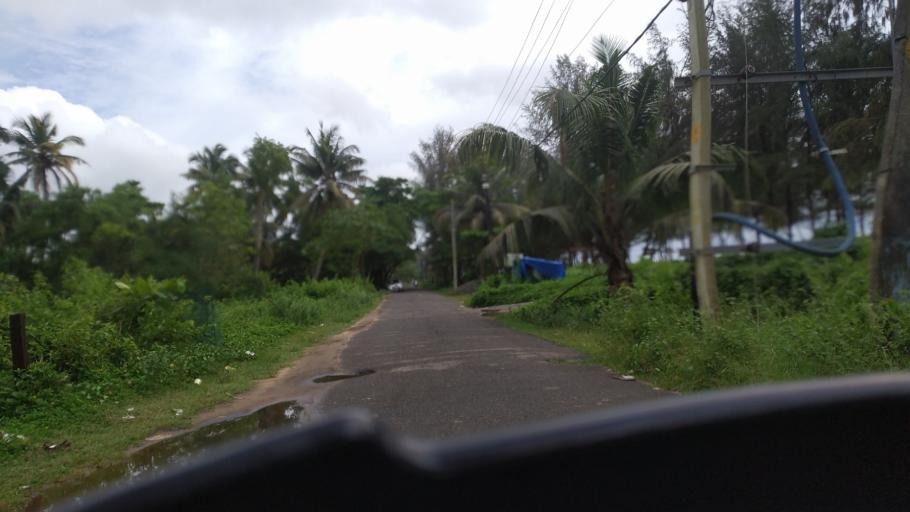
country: IN
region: Kerala
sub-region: Ernakulam
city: Elur
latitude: 10.1093
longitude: 76.1878
